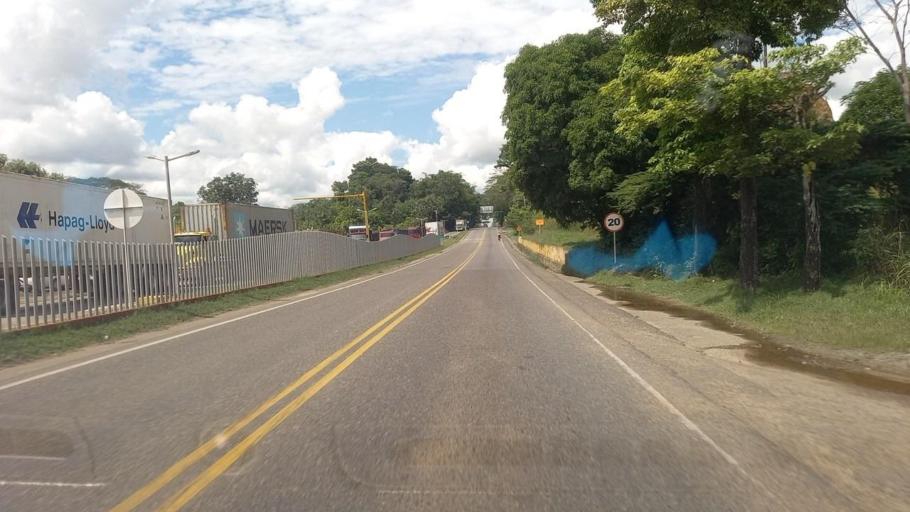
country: CO
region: Santander
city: Barrancabermeja
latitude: 7.1248
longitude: -73.5828
